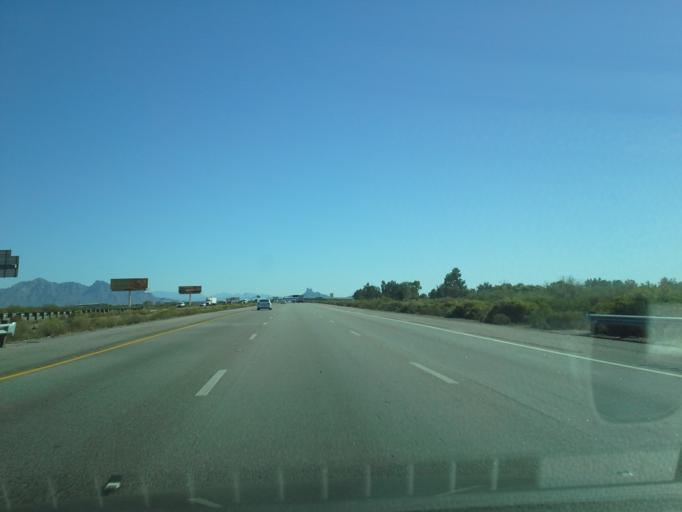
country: US
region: Arizona
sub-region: Pinal County
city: Eloy
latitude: 32.7712
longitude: -111.6099
